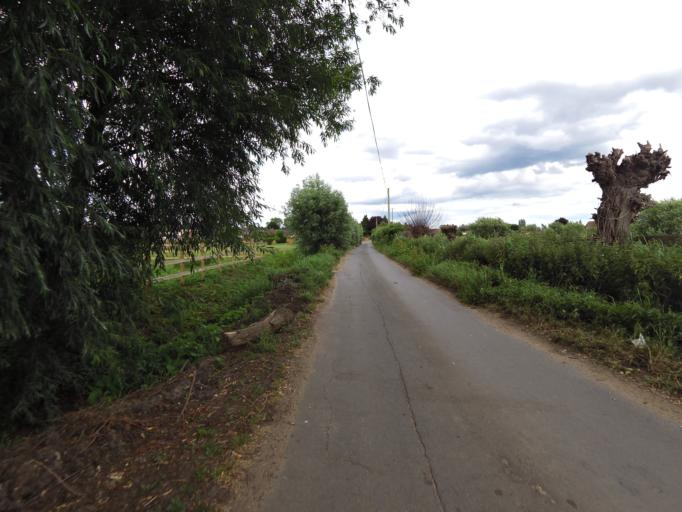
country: GB
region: England
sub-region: Suffolk
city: Beccles
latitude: 52.4695
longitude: 1.5442
